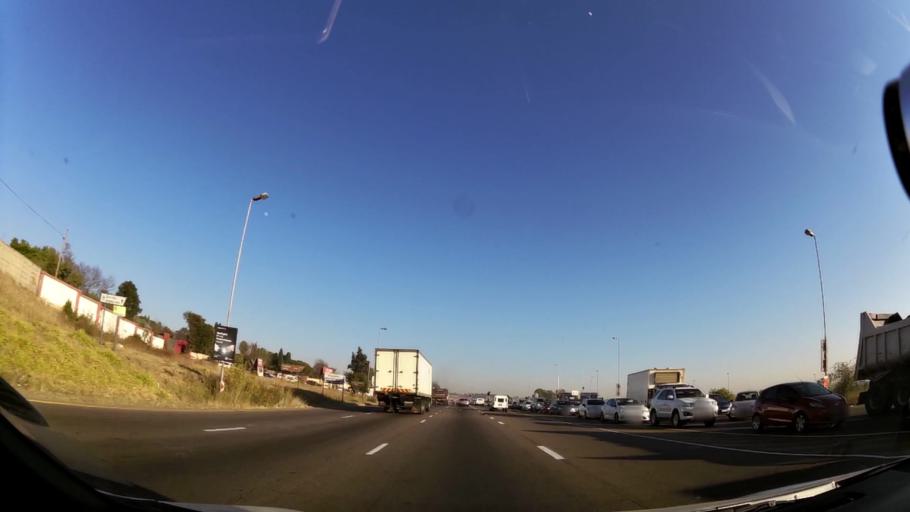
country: ZA
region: Gauteng
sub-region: City of Johannesburg Metropolitan Municipality
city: Midrand
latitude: -25.9509
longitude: 28.1246
